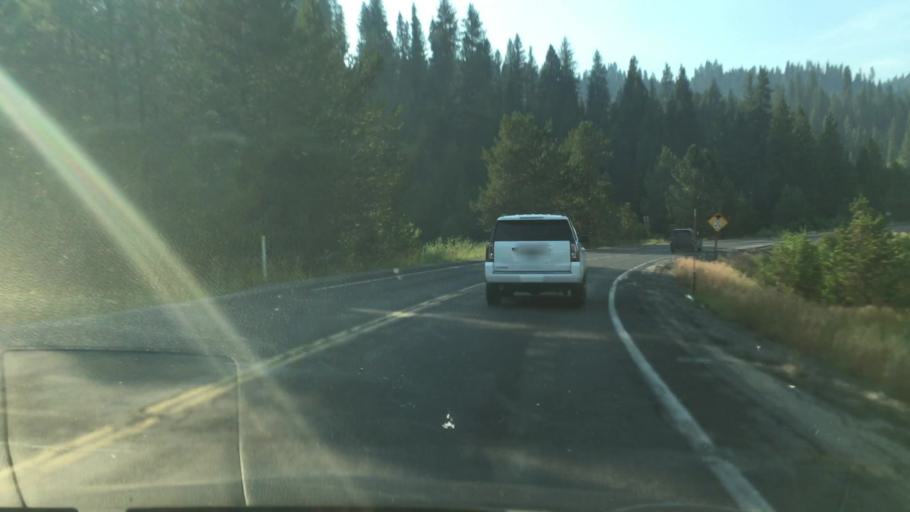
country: US
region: Idaho
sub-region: Valley County
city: Cascade
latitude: 44.2979
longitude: -116.0883
